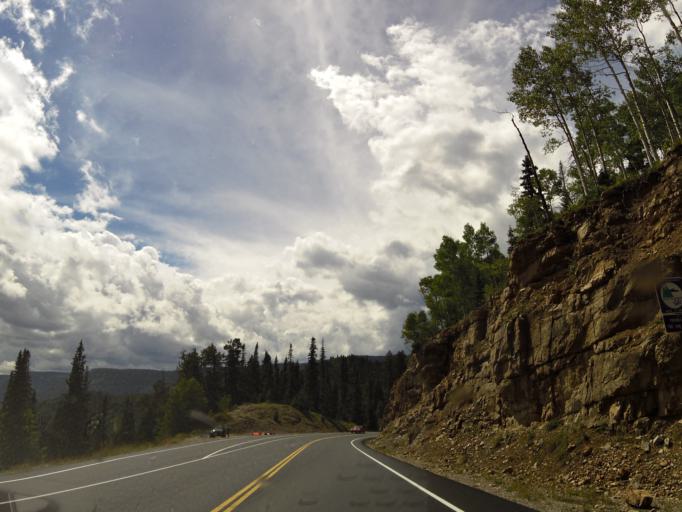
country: US
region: Colorado
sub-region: San Juan County
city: Silverton
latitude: 37.6794
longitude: -107.7919
